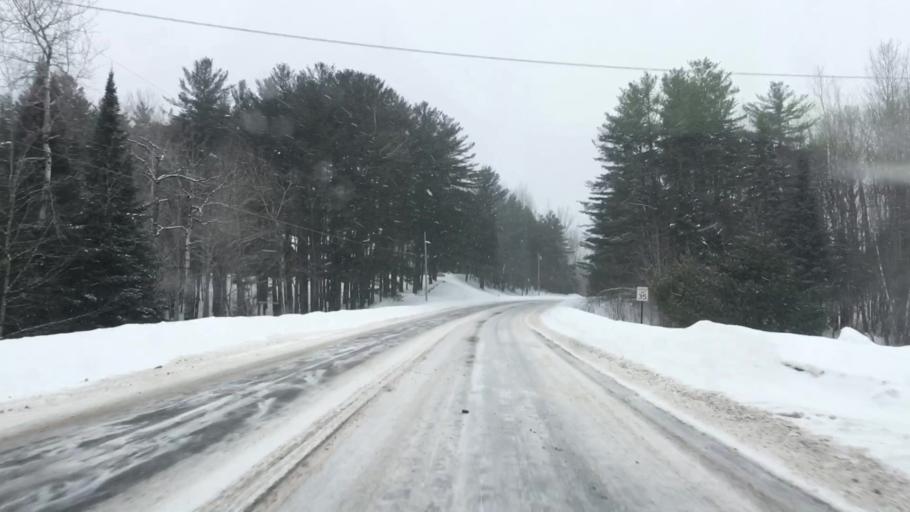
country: US
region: Maine
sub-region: Penobscot County
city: Medway
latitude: 45.5219
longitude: -68.3532
